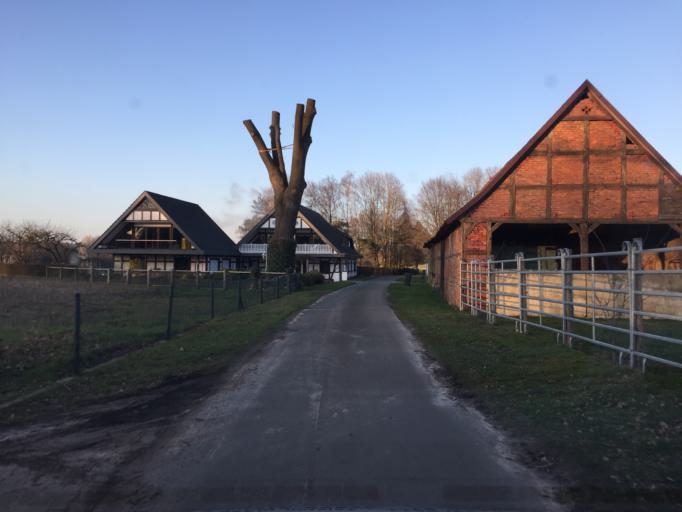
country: DE
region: Lower Saxony
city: Varrel
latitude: 52.6573
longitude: 8.7452
